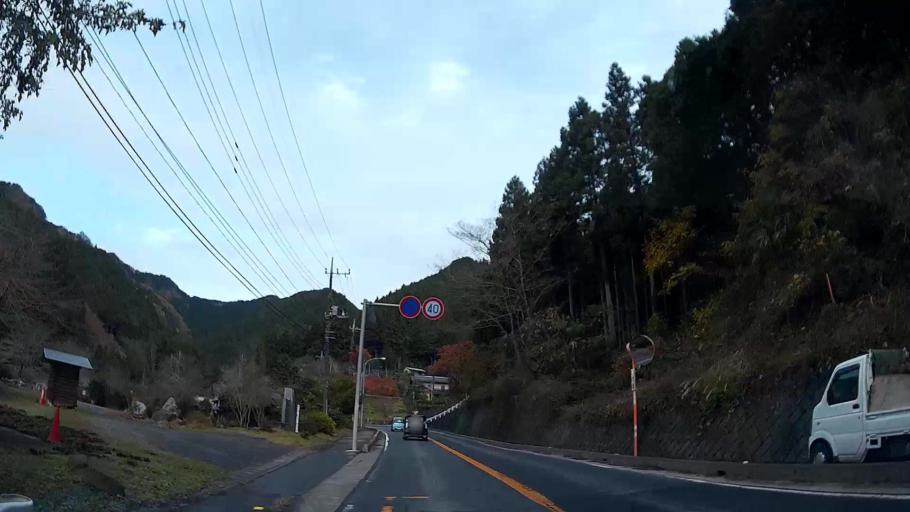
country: JP
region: Saitama
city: Chichibu
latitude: 35.9463
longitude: 139.1807
